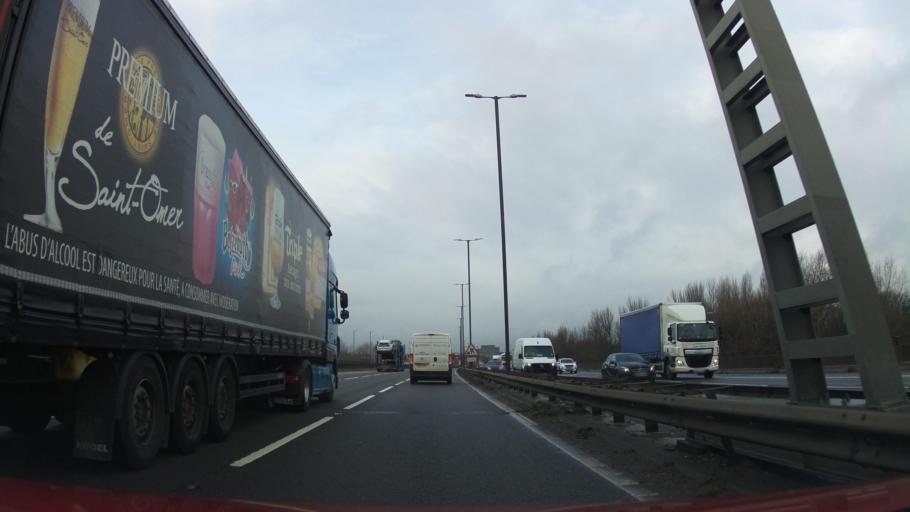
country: GB
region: England
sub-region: Walsall
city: Walsall
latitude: 52.5677
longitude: -2.0006
